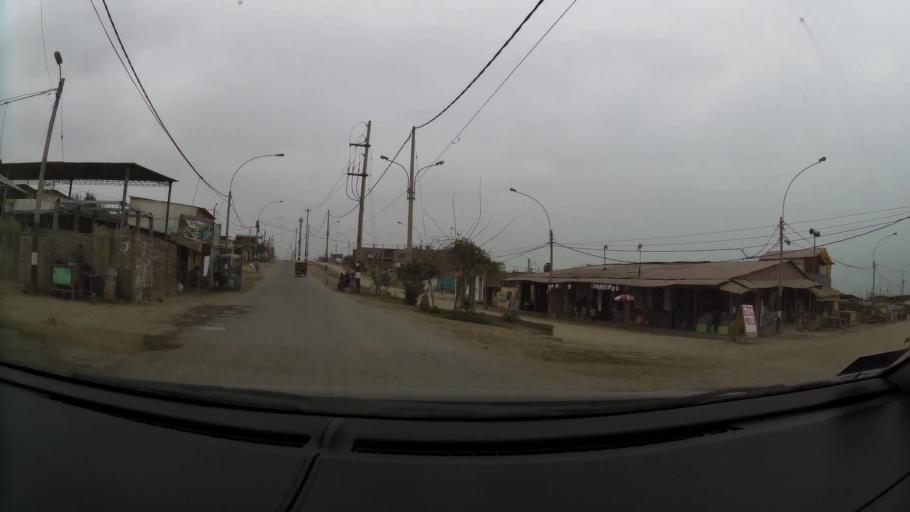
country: PE
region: Lima
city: Ventanilla
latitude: -11.8472
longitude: -77.1478
